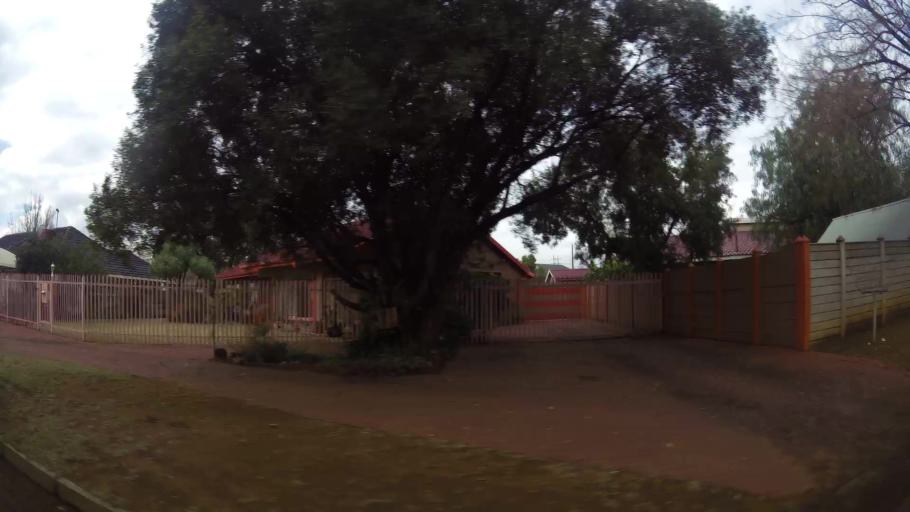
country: ZA
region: Gauteng
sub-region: Sedibeng District Municipality
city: Vereeniging
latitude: -26.6452
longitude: 27.9752
